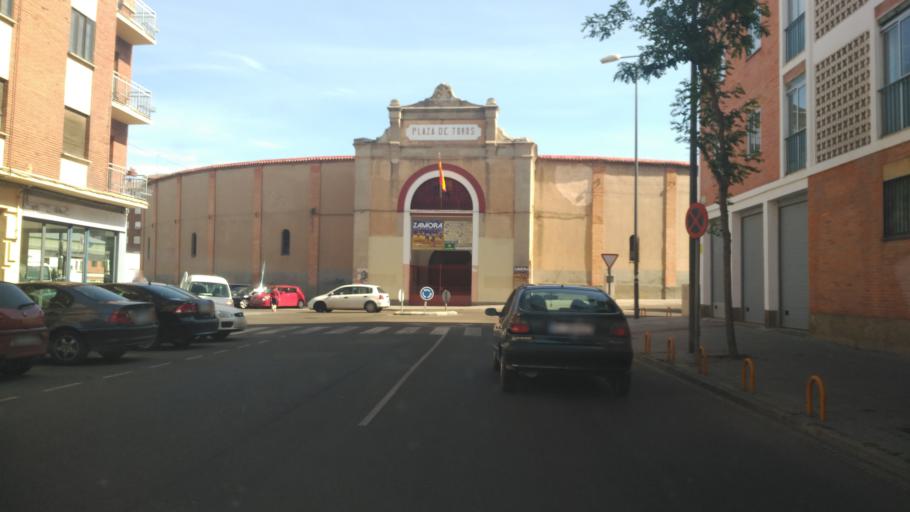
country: ES
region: Castille and Leon
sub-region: Provincia de Zamora
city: Zamora
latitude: 41.5094
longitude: -5.7455
